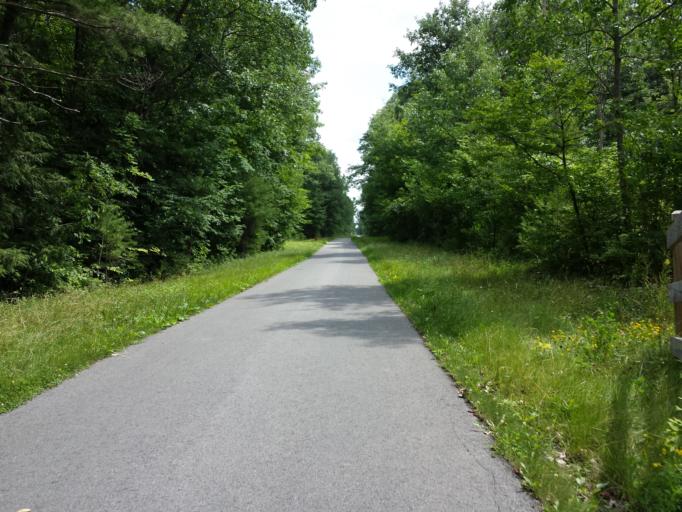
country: US
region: New York
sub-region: Saratoga County
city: Ballston Spa
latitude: 42.9874
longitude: -73.8418
